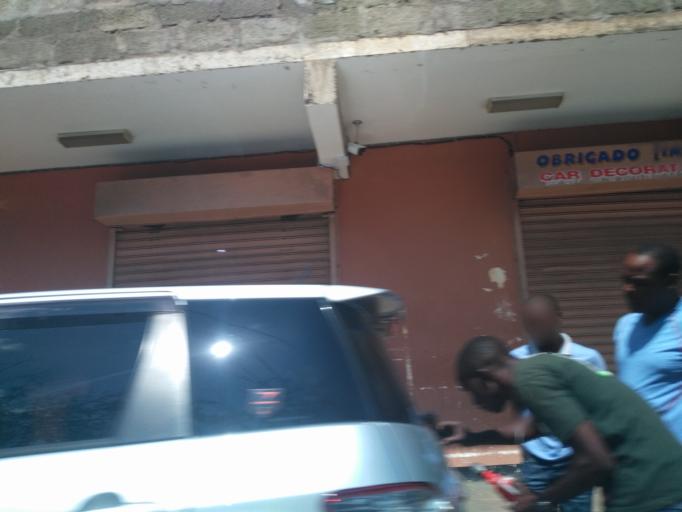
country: TZ
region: Arusha
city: Arusha
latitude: -3.3696
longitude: 36.6817
